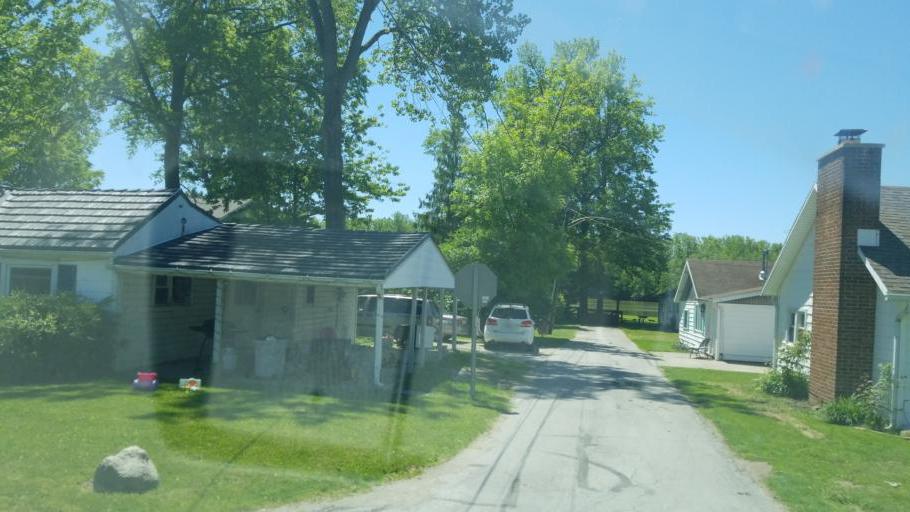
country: US
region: Ohio
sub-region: Shelby County
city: Fort Loramie
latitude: 40.3689
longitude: -84.3441
